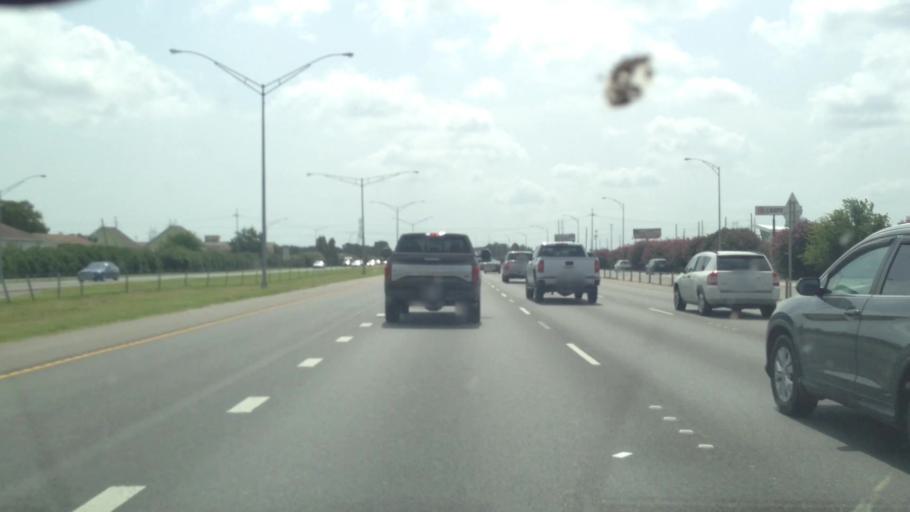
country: US
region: Louisiana
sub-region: Jefferson Parish
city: Kenner
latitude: 30.0087
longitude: -90.2313
